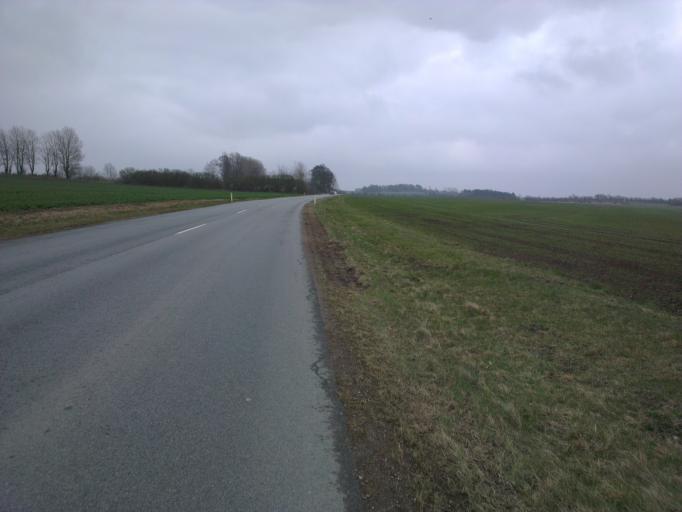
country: DK
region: Capital Region
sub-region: Frederikssund Kommune
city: Jaegerspris
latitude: 55.8325
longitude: 12.0067
